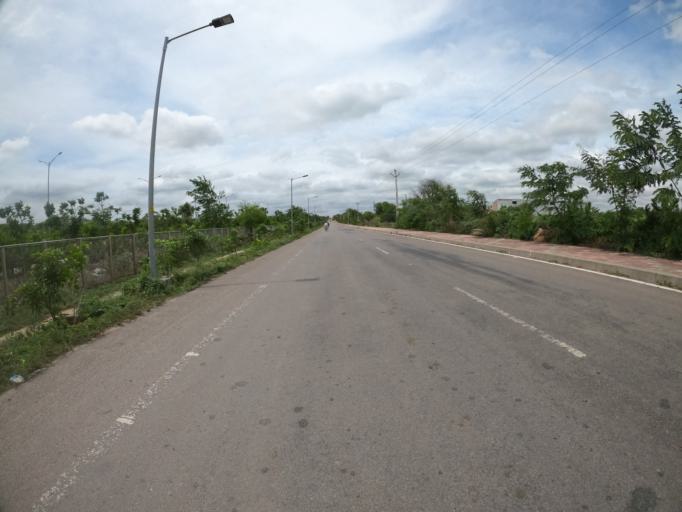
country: IN
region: Telangana
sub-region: Hyderabad
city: Hyderabad
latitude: 17.2953
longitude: 78.3801
